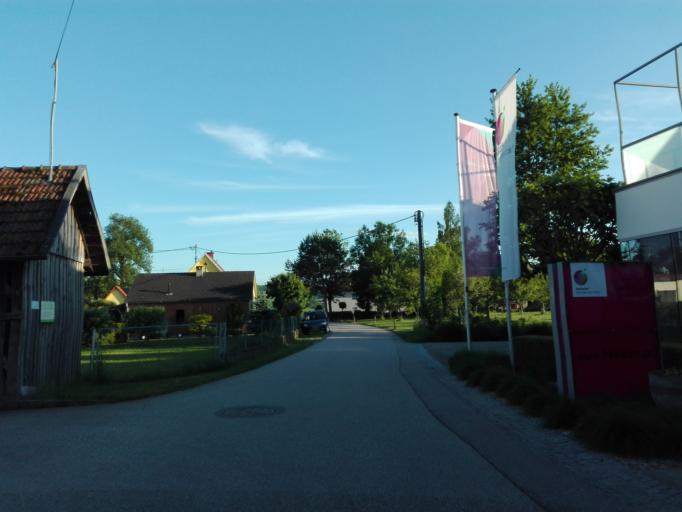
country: AT
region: Upper Austria
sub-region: Politischer Bezirk Urfahr-Umgebung
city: Goldworth
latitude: 48.2860
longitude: 14.0651
